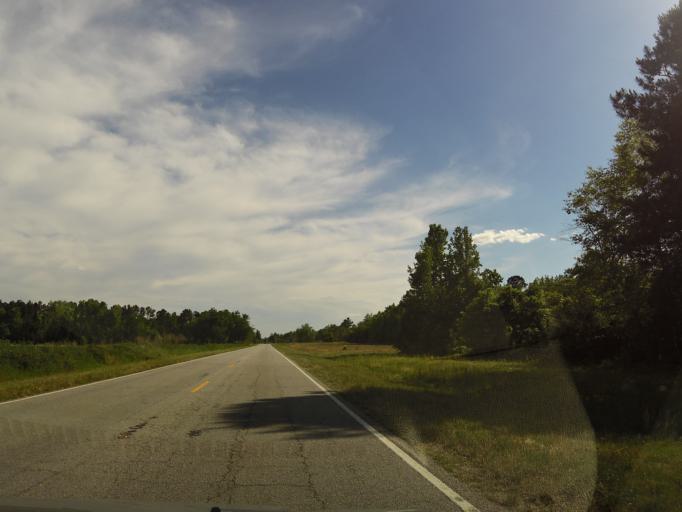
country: US
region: South Carolina
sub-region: Allendale County
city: Fairfax
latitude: 33.0431
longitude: -81.2203
